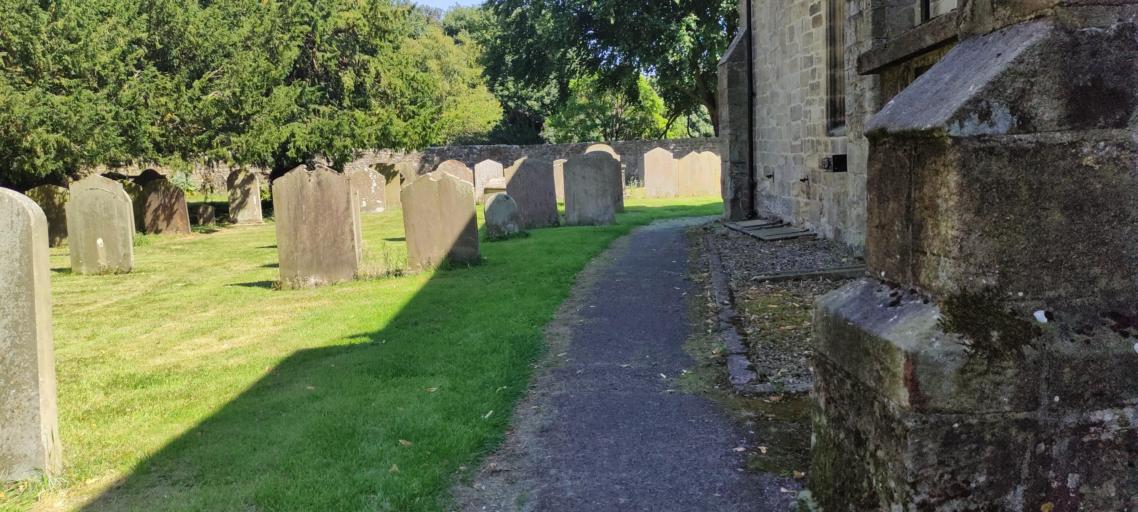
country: GB
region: England
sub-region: North Yorkshire
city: Bedale
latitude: 54.2214
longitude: -1.6537
